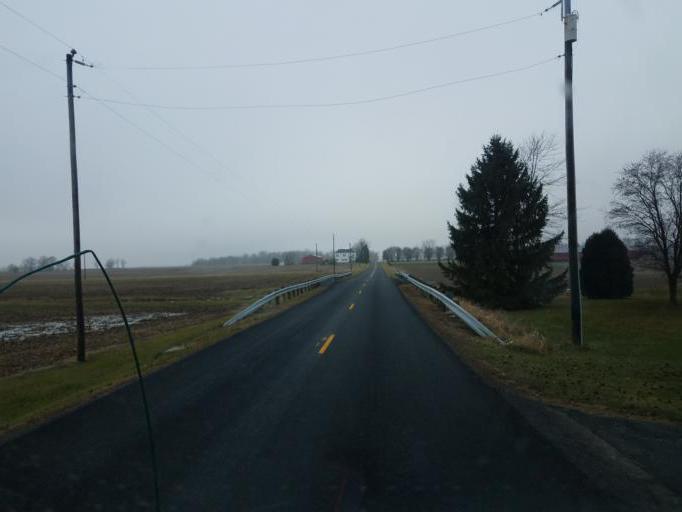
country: US
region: Ohio
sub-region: Champaign County
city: North Lewisburg
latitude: 40.2372
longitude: -83.5443
